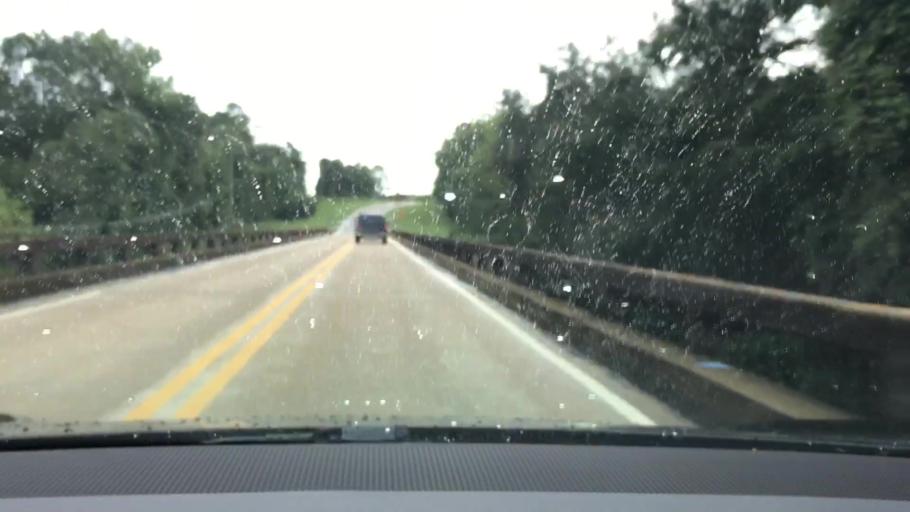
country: US
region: Alabama
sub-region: Geneva County
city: Samson
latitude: 31.0442
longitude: -86.1015
